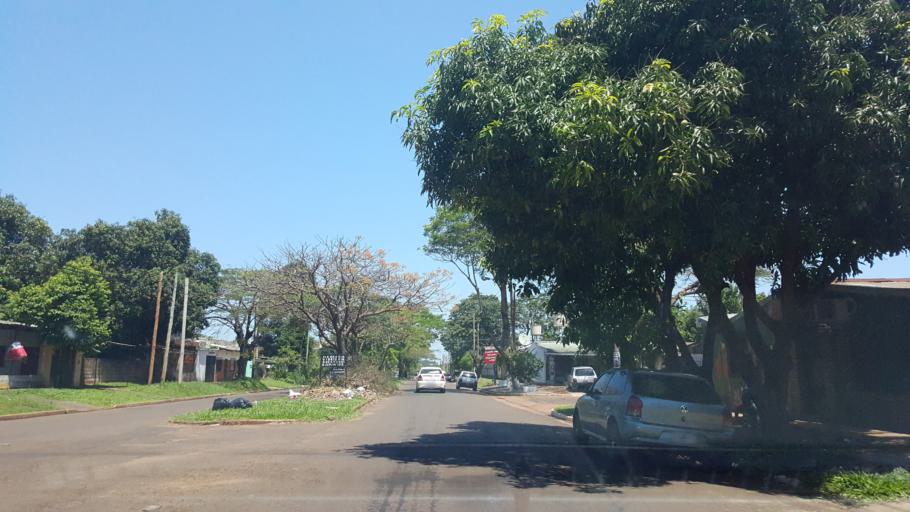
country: AR
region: Misiones
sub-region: Departamento de Capital
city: Posadas
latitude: -27.3788
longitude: -55.9258
